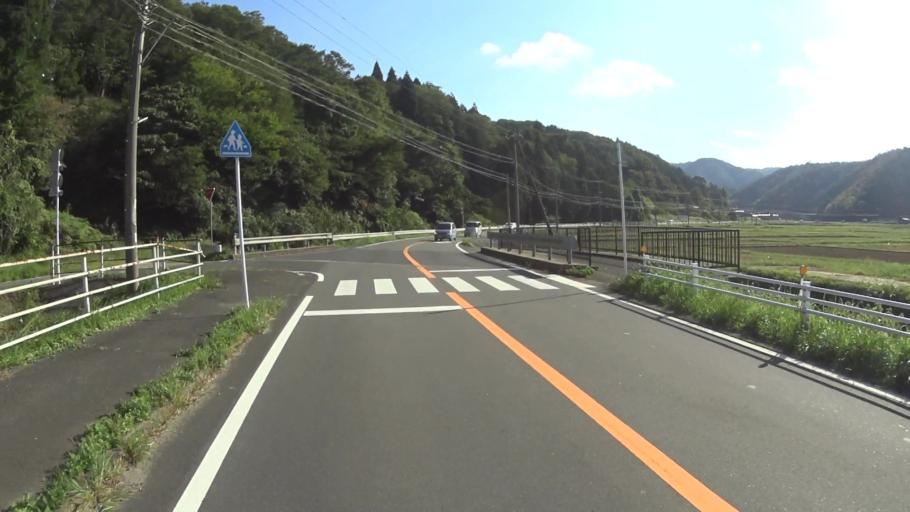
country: JP
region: Kyoto
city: Miyazu
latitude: 35.6633
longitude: 135.0235
